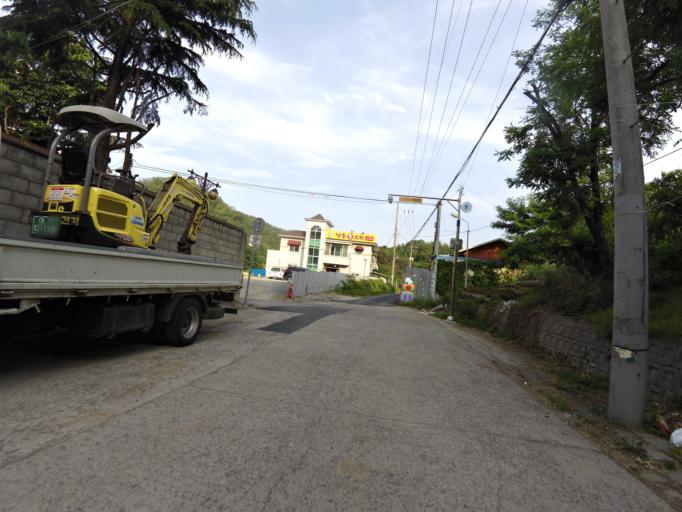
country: KR
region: Daegu
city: Daegu
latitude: 35.8615
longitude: 128.6490
